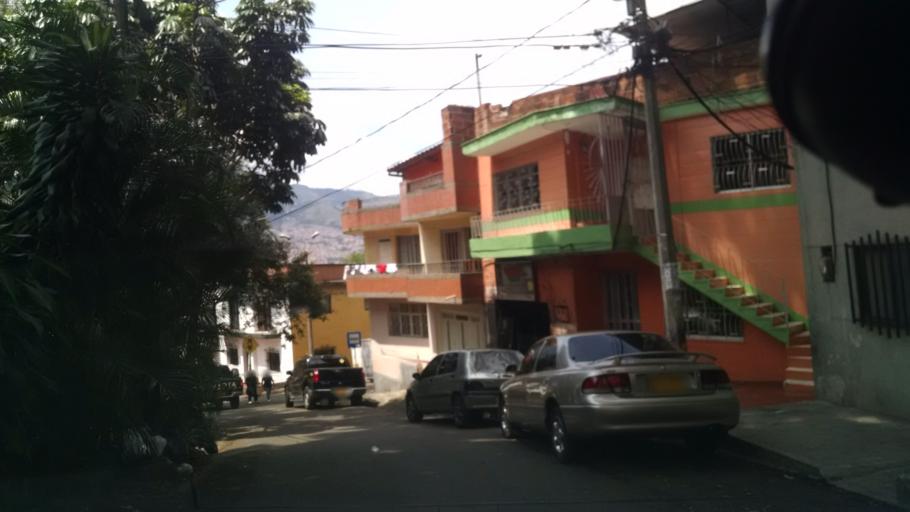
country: CO
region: Antioquia
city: Medellin
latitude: 6.2685
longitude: -75.5551
